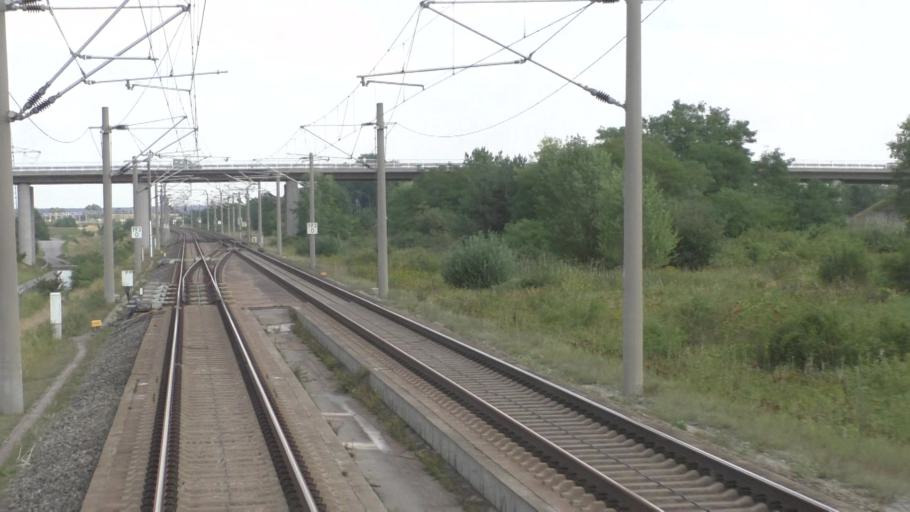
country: DE
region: Saxony-Anhalt
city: Schonhausen
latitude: 52.5927
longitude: 12.0274
